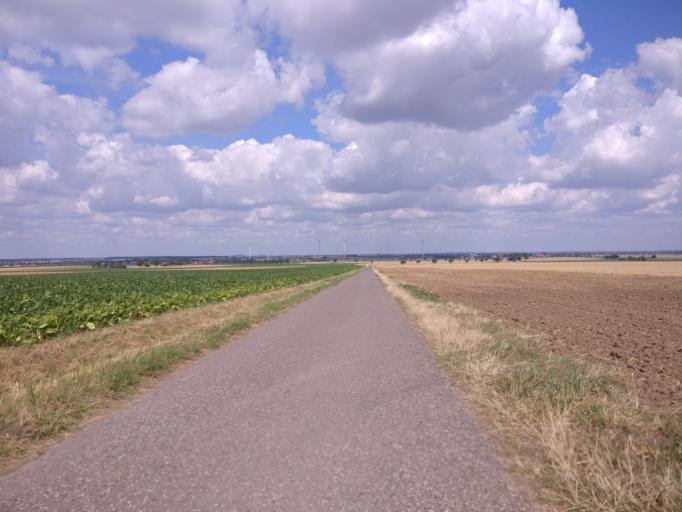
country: DE
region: Lower Saxony
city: Hildesheim
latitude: 52.1408
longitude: 10.0258
